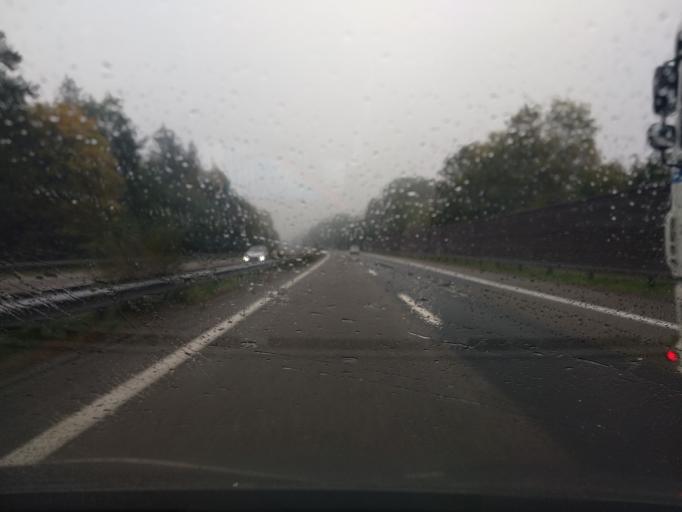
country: CH
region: Saint Gallen
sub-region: Wahlkreis Wil
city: Zuzwil
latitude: 47.4585
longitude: 9.1202
